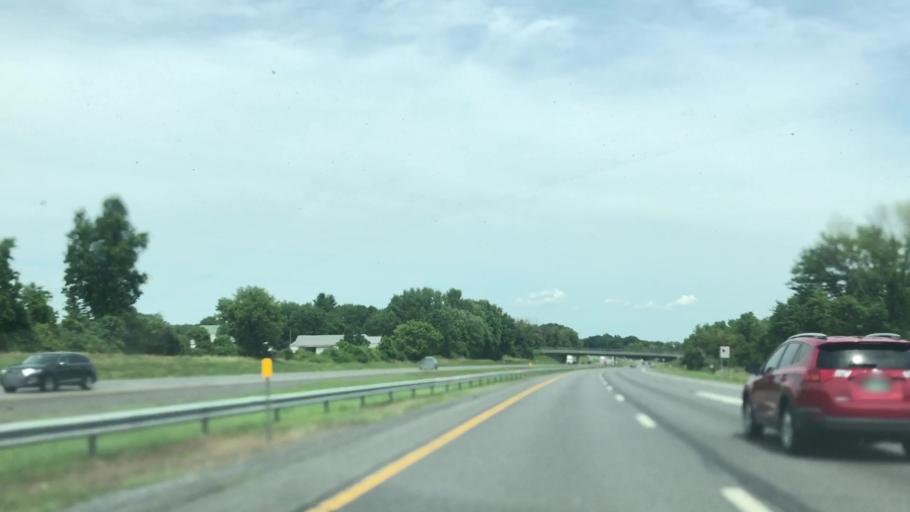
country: US
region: New York
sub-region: Rensselaer County
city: Castleton-on-Hudson
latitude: 42.5376
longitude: -73.7829
